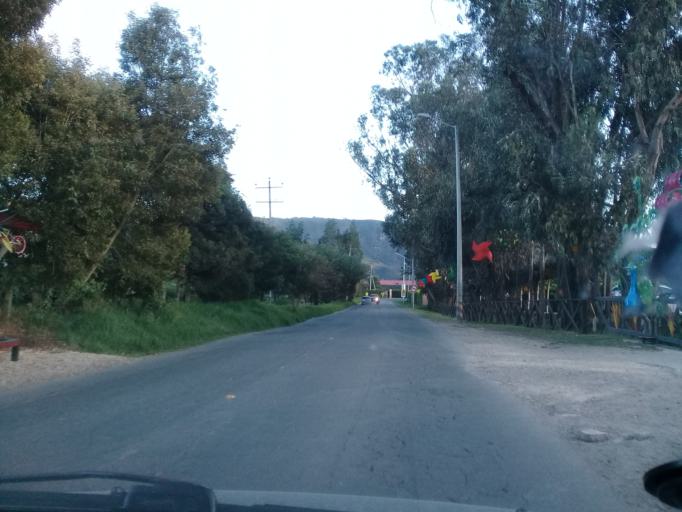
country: CO
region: Cundinamarca
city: Tenjo
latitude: 4.8562
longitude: -74.1344
